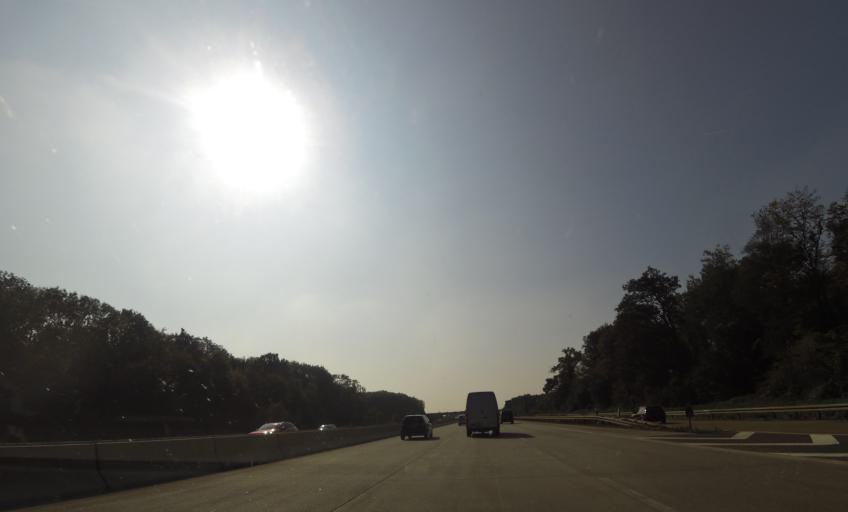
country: DE
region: Baden-Wuerttemberg
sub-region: Karlsruhe Region
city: Forst
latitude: 49.1519
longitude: 8.5623
